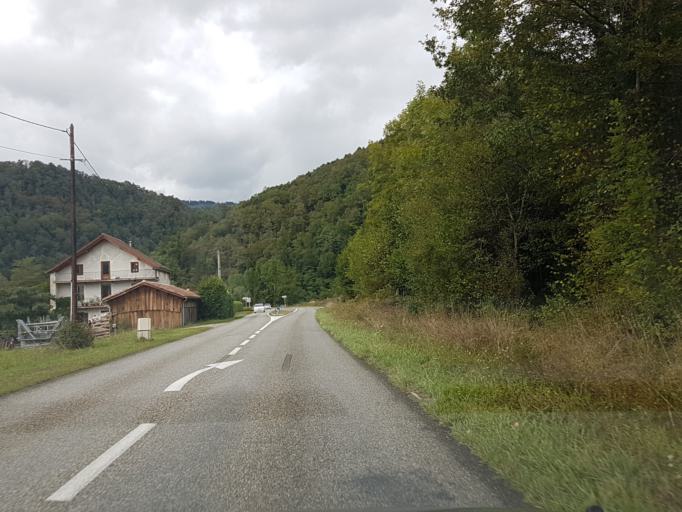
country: FR
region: Midi-Pyrenees
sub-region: Departement de l'Ariege
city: Saint-Girons
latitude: 42.8979
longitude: 1.2146
